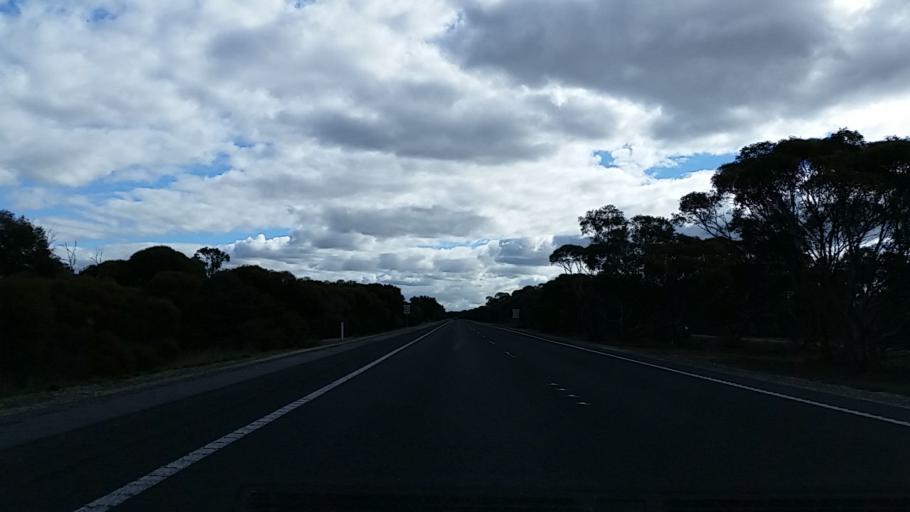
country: AU
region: South Australia
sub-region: Mount Barker
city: Callington
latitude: -35.1350
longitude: 139.1239
